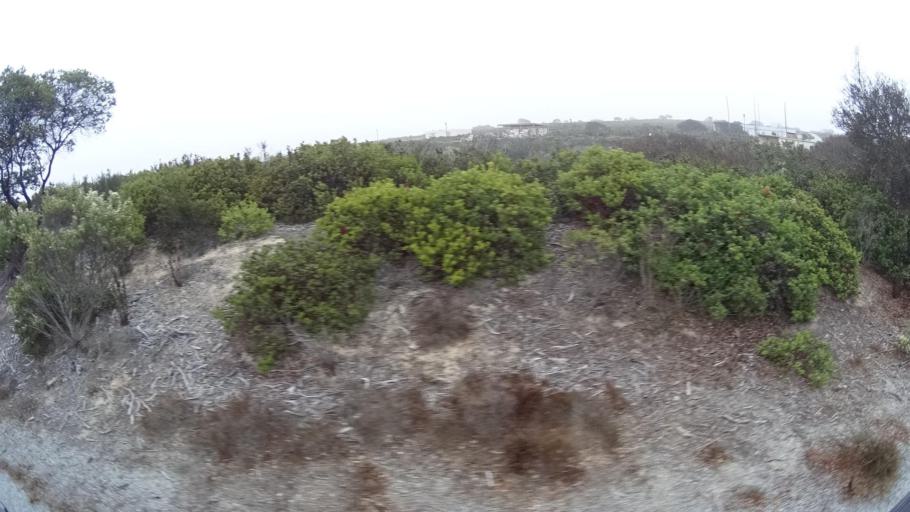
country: US
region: California
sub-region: Monterey County
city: Marina
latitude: 36.6417
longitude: -121.7348
